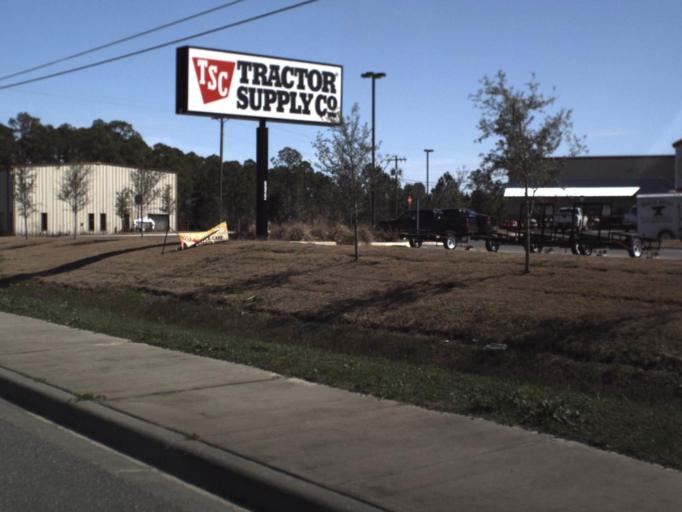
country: US
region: Florida
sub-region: Bay County
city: Lynn Haven
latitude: 30.2760
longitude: -85.6386
